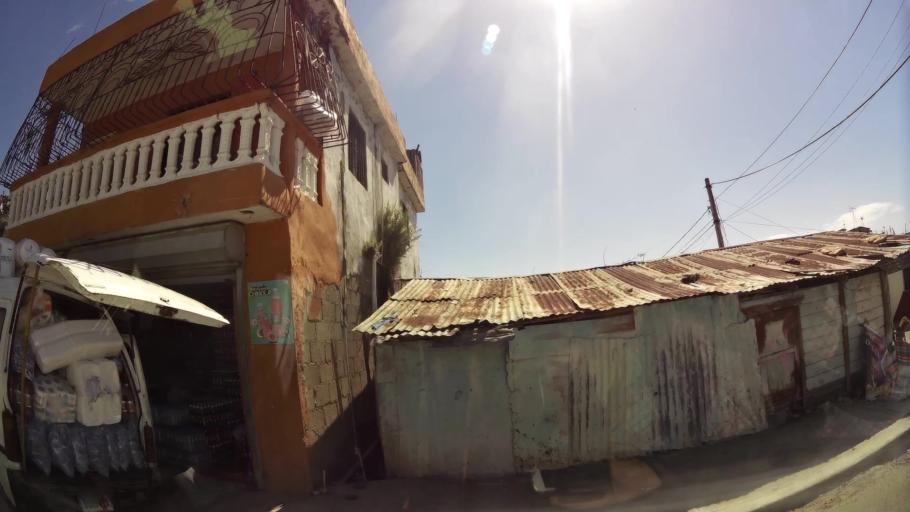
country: DO
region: San Cristobal
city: San Cristobal
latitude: 18.4283
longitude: -70.1324
